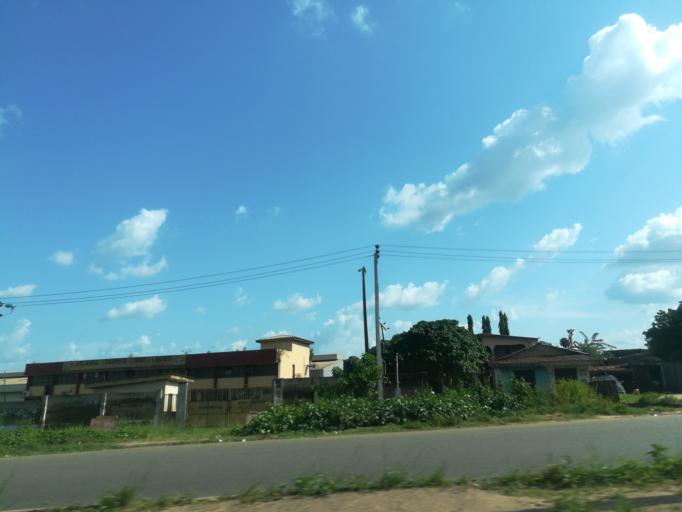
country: NG
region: Oyo
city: Egbeda
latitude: 7.4284
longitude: 4.0016
